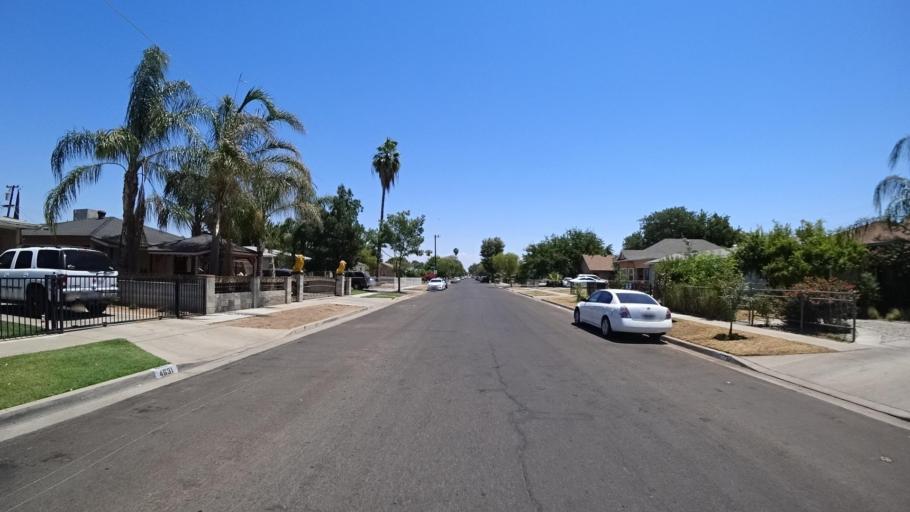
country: US
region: California
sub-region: Fresno County
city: Fresno
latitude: 36.7332
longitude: -119.7441
